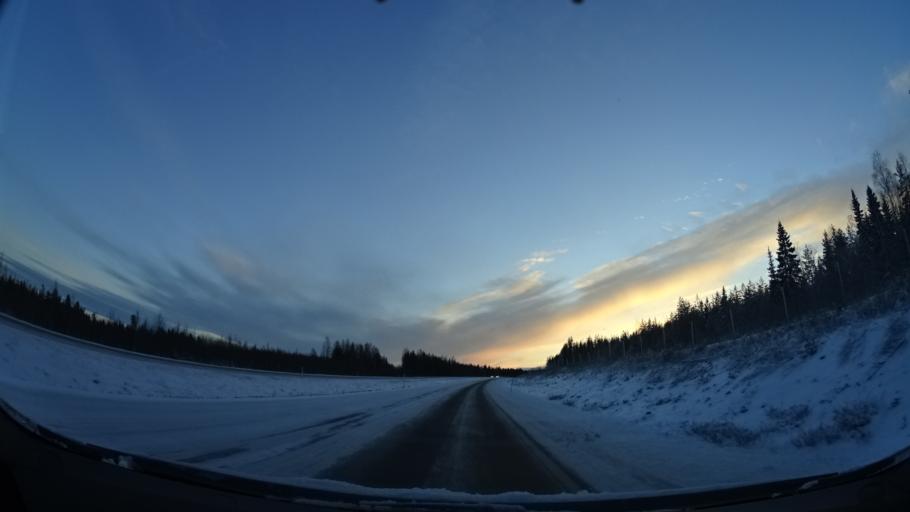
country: SE
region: Vaesterbotten
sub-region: Skelleftea Kommun
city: Kage
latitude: 64.8106
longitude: 21.0321
